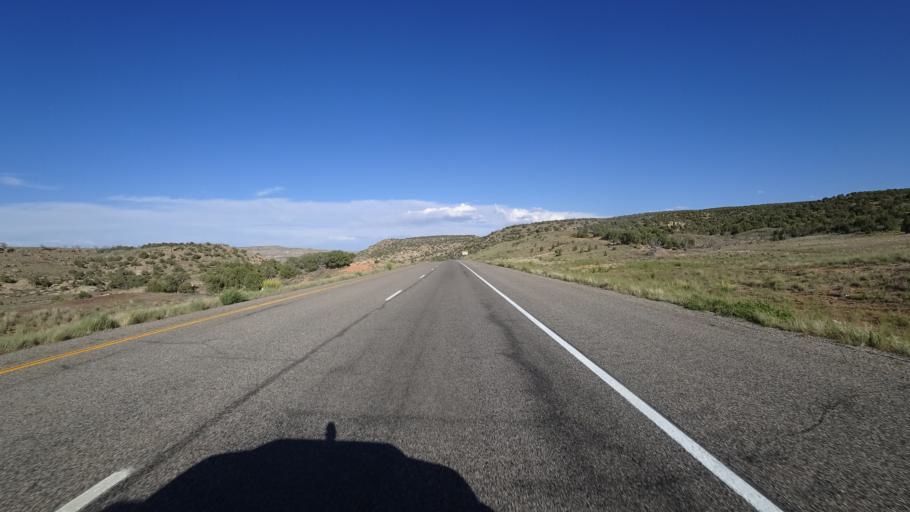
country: US
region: Colorado
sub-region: Mesa County
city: Loma
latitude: 39.1888
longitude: -109.0397
